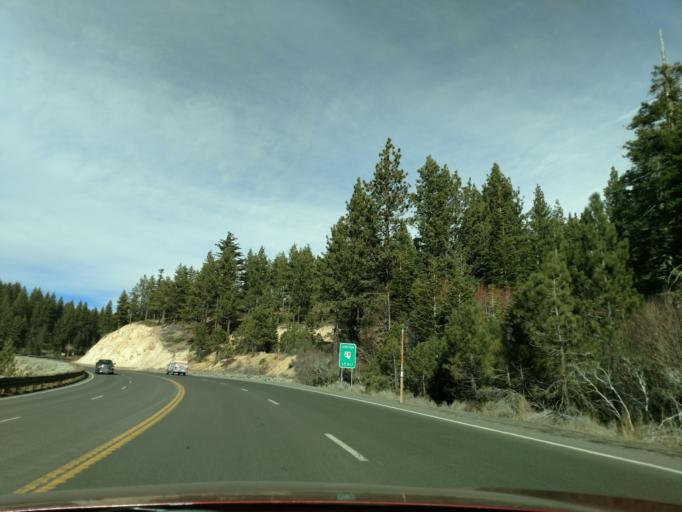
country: US
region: Nevada
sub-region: Douglas County
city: Kingsbury
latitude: 39.0928
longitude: -119.9102
